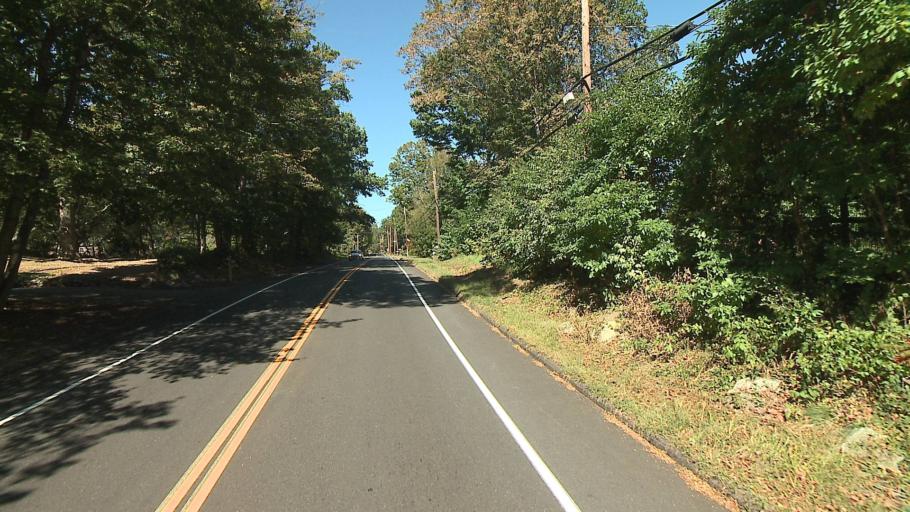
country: US
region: Connecticut
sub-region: New Haven County
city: Orange
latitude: 41.2653
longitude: -73.0168
